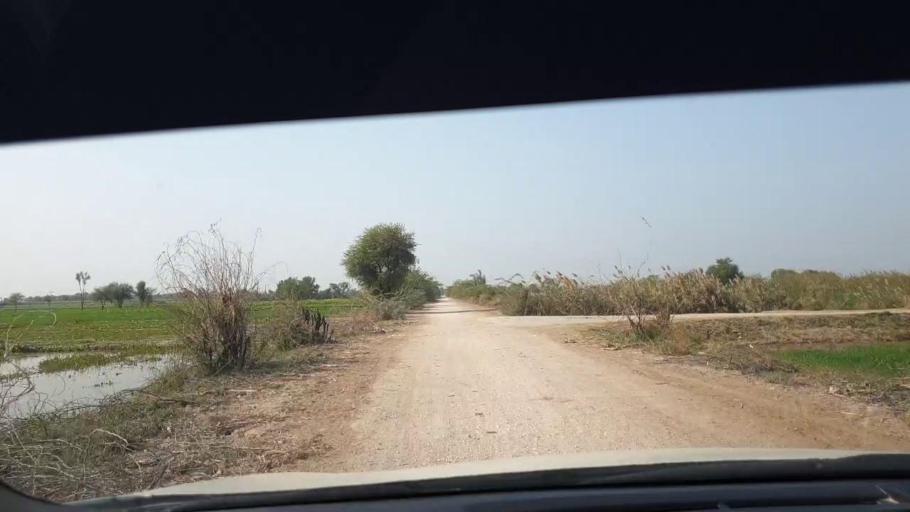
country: PK
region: Sindh
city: Tando Adam
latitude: 25.8416
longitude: 68.7119
